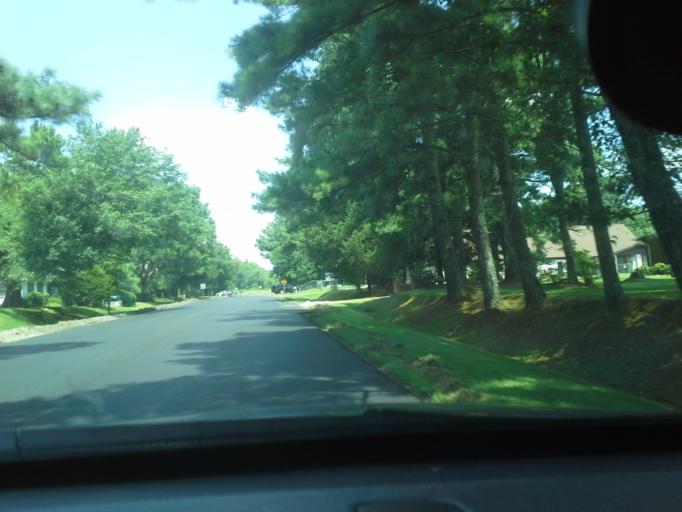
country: US
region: North Carolina
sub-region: Washington County
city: Plymouth
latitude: 35.8663
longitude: -76.7409
